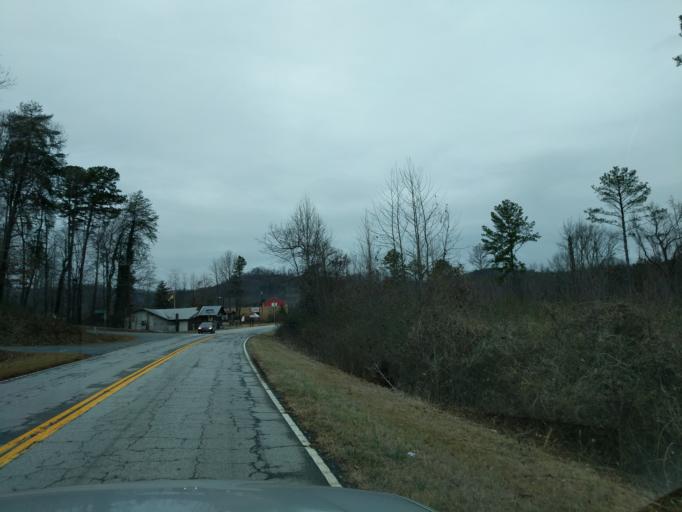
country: US
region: South Carolina
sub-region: Oconee County
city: Walhalla
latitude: 34.7869
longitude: -83.1146
